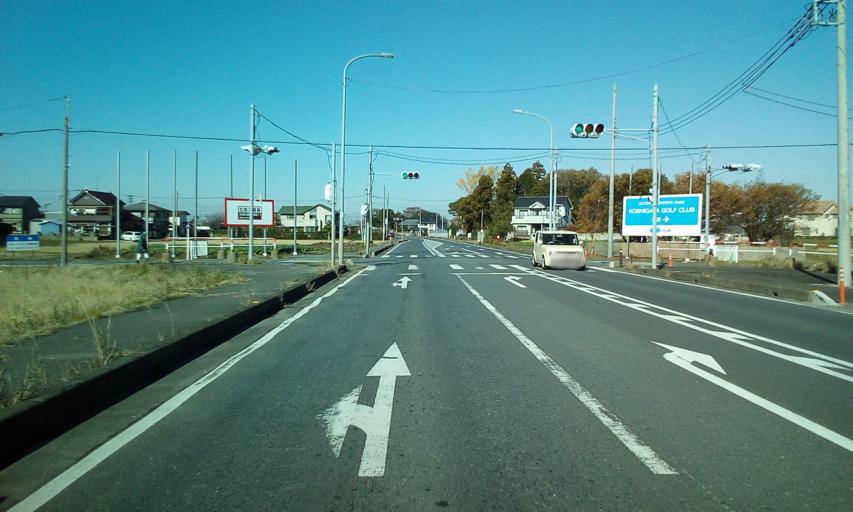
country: JP
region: Chiba
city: Nagareyama
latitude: 35.8872
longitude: 139.8843
